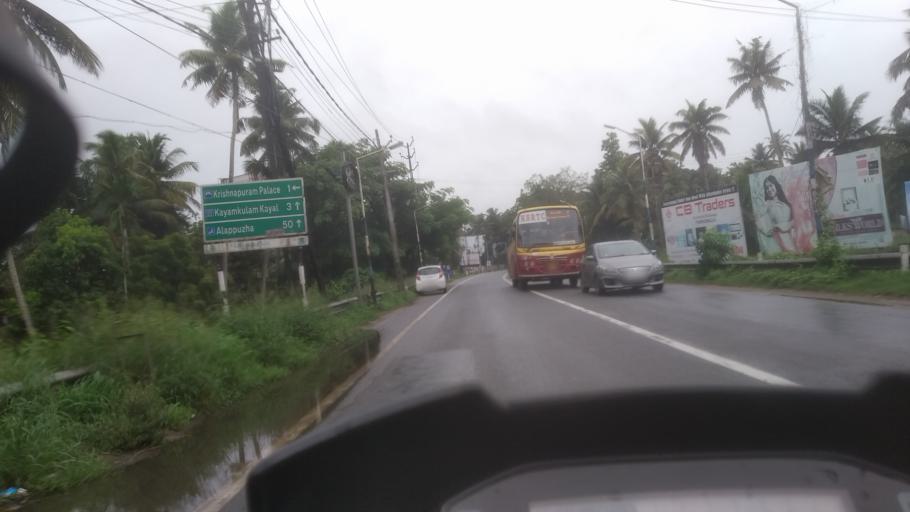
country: IN
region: Kerala
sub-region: Alappuzha
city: Kayankulam
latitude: 9.1530
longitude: 76.5114
